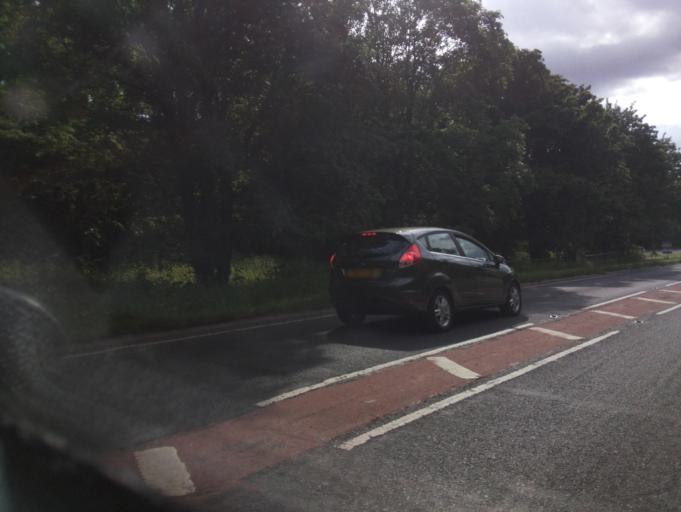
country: GB
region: England
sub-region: Worcestershire
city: Pershore
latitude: 52.1029
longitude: -2.0693
